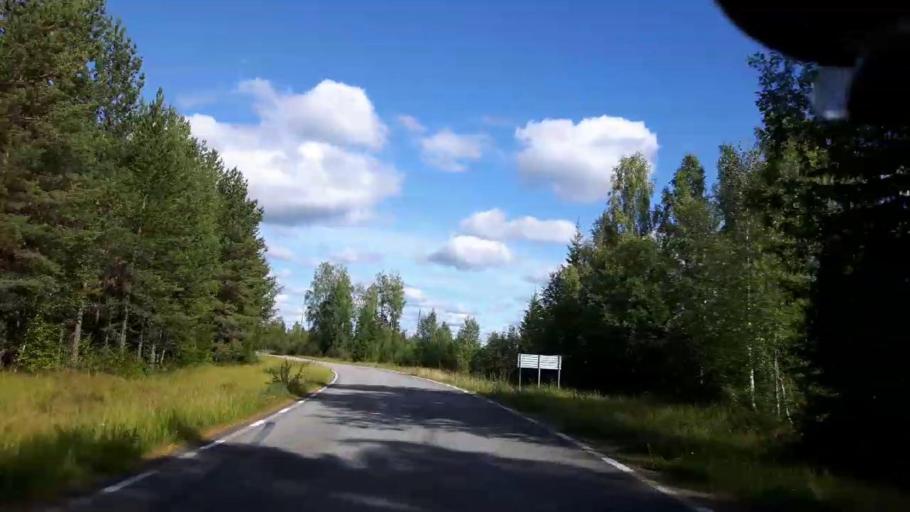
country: SE
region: Jaemtland
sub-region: OEstersunds Kommun
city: Brunflo
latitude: 63.2077
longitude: 15.2475
